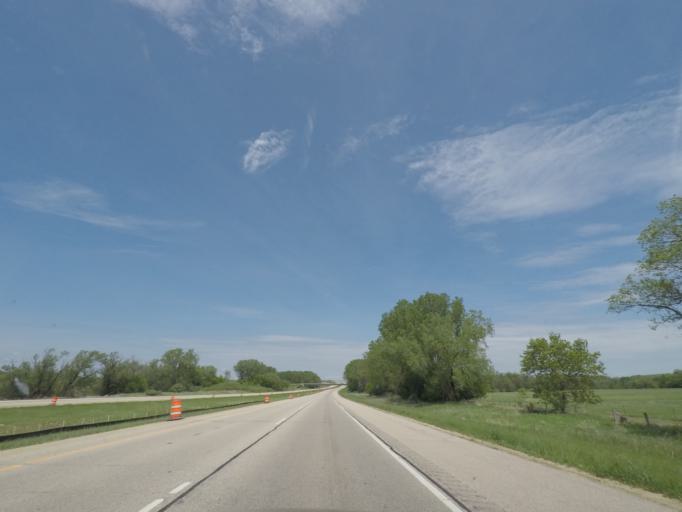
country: US
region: Wisconsin
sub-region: Dane County
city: Oregon
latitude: 42.9965
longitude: -89.3856
